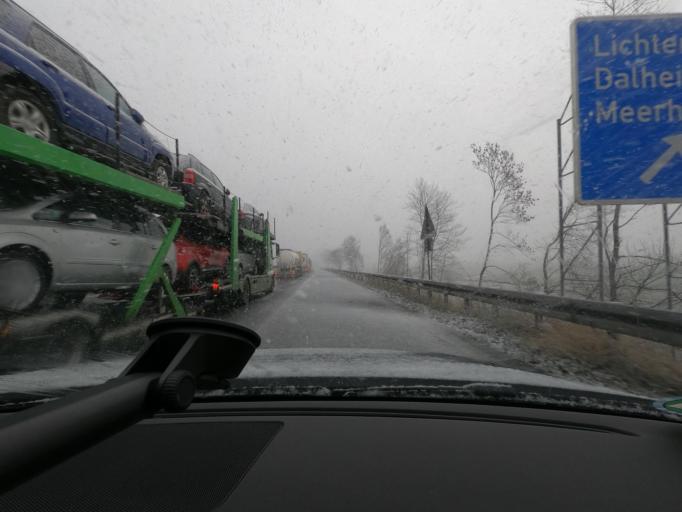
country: DE
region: North Rhine-Westphalia
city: Marsberg
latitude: 51.5421
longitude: 8.8328
